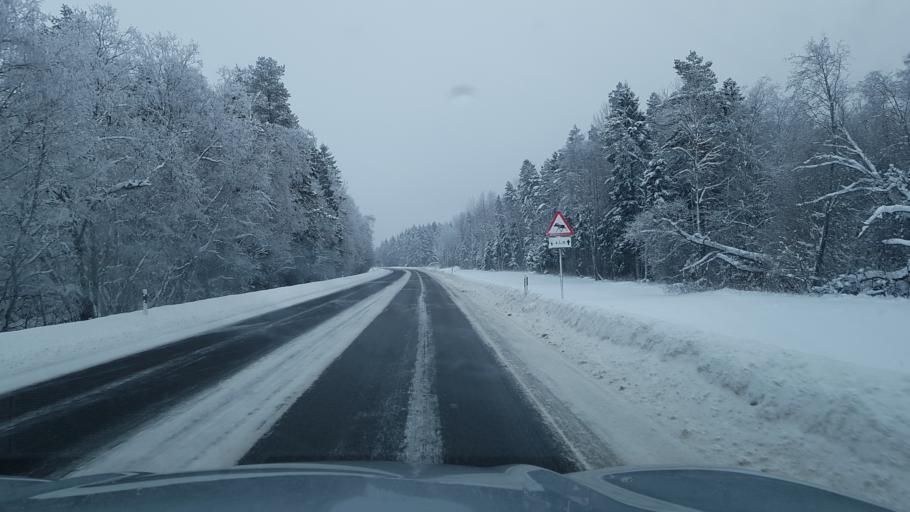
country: EE
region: Ida-Virumaa
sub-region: Johvi vald
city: Johvi
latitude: 59.3079
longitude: 27.3930
